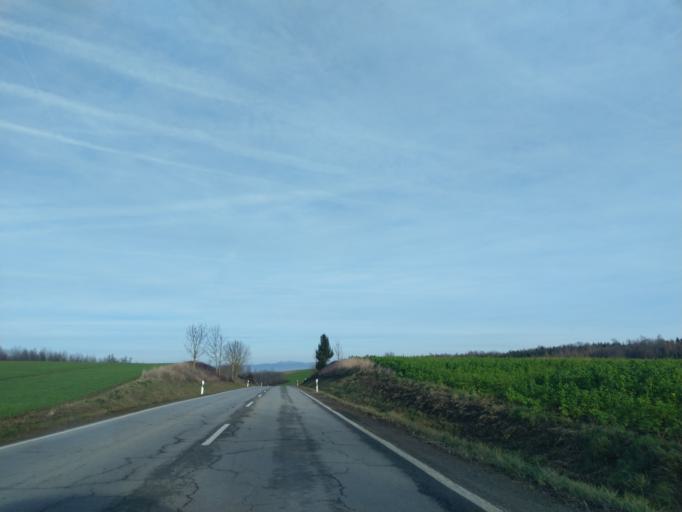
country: DE
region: Bavaria
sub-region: Lower Bavaria
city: Wallerfing
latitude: 48.6738
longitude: 12.8757
